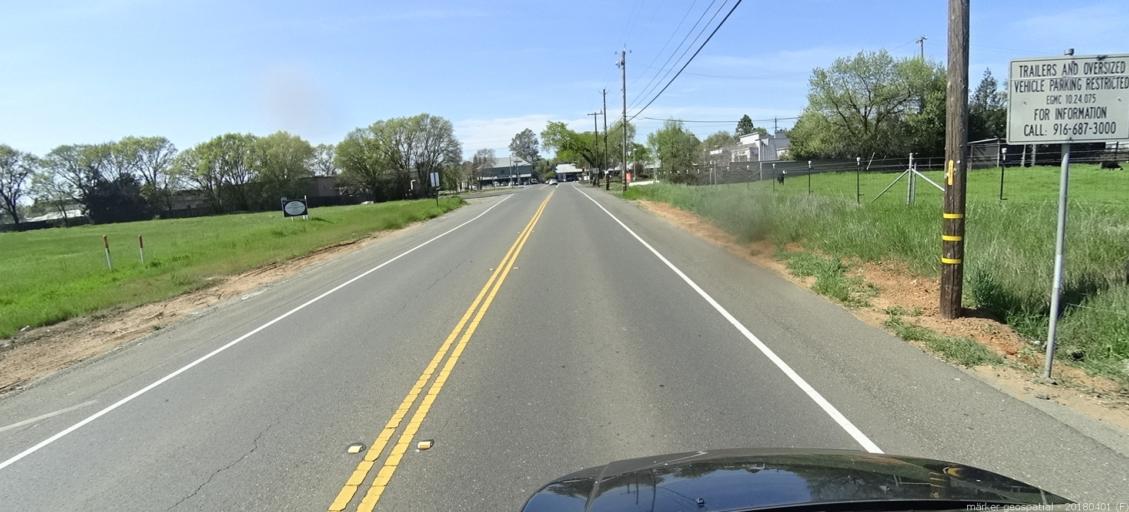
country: US
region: California
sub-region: Sacramento County
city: Wilton
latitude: 38.4299
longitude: -121.2991
